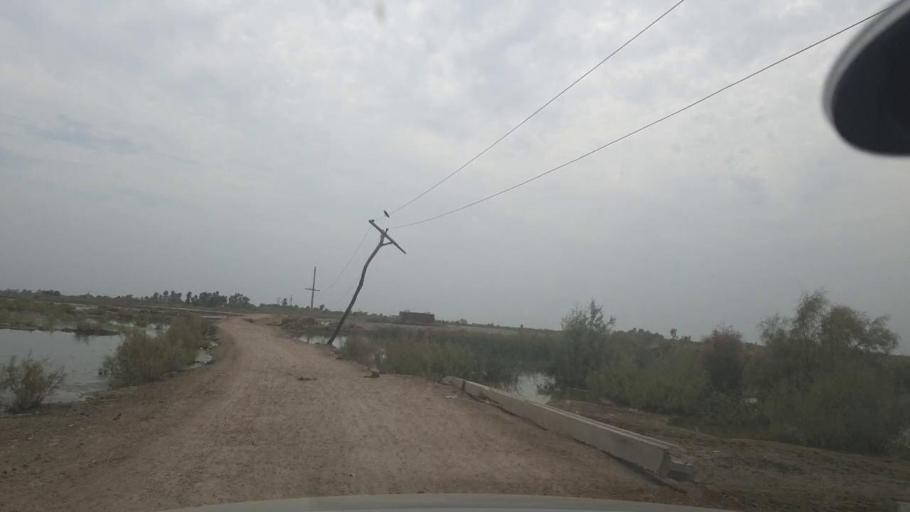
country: PK
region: Balochistan
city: Mehrabpur
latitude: 28.0484
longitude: 68.1359
